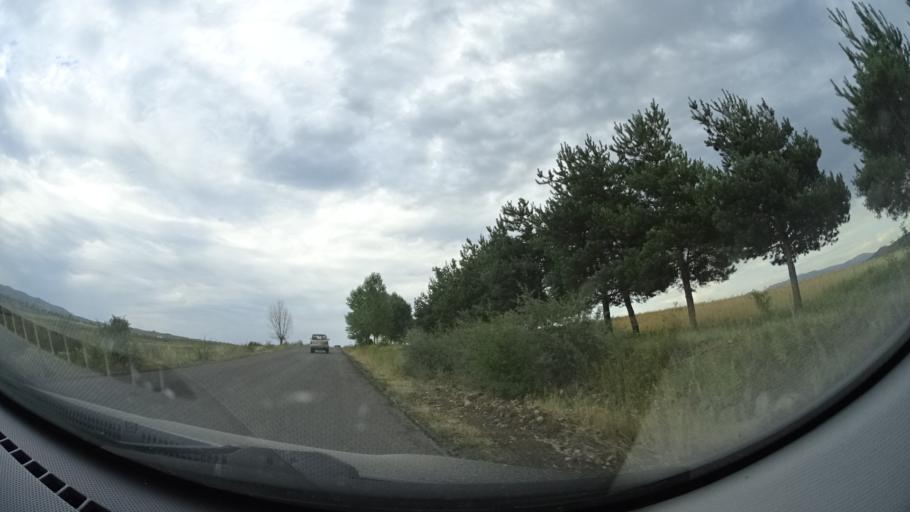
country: GE
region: Samtskhe-Javakheti
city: Adigeni
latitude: 41.6640
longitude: 42.7656
